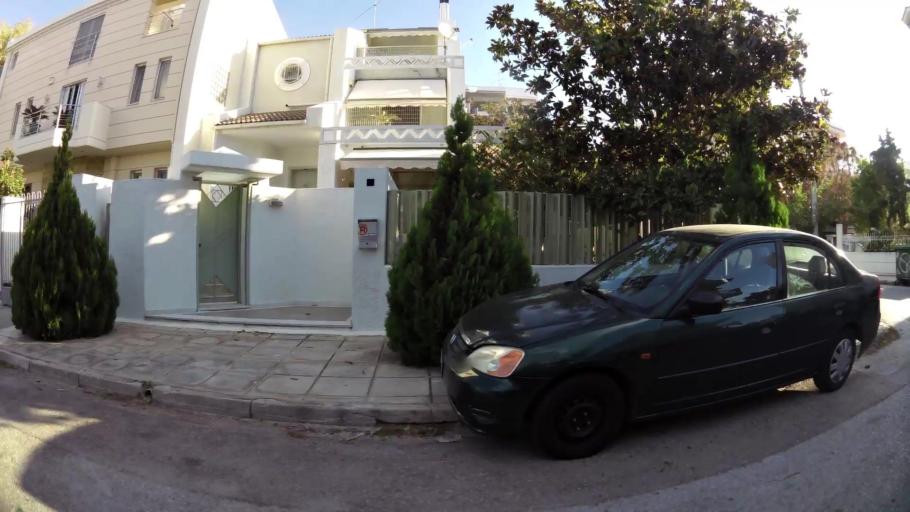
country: GR
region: Attica
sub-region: Nomarchia Athinas
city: Elliniko
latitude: 37.8817
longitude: 23.7470
